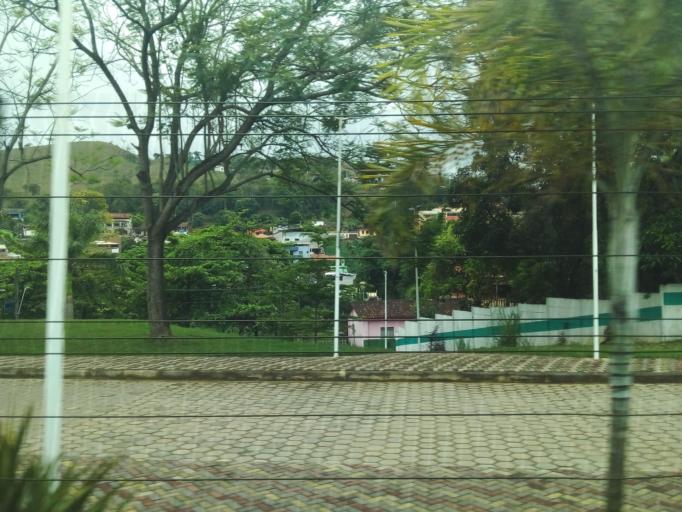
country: BR
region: Minas Gerais
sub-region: Rio Piracicaba
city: Rio Piracicaba
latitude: -19.9315
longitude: -43.1725
